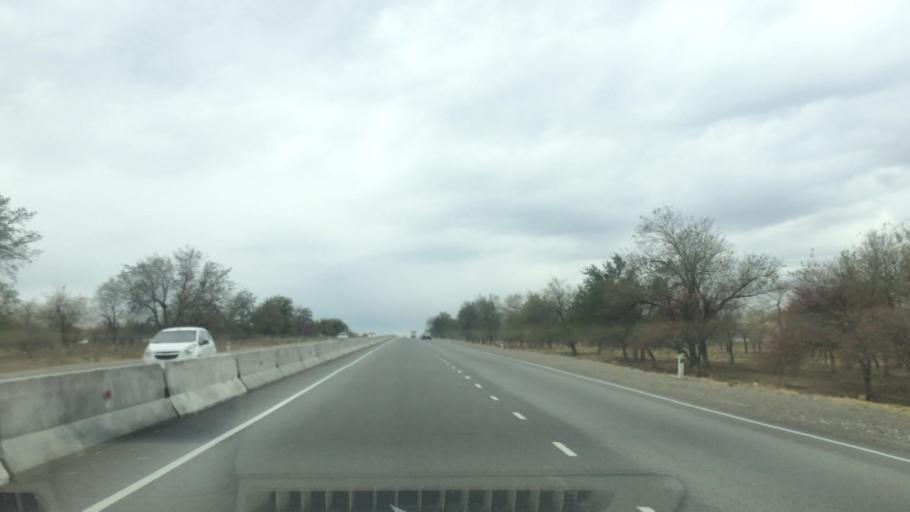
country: UZ
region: Samarqand
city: Bulung'ur
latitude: 39.9336
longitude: 67.5238
